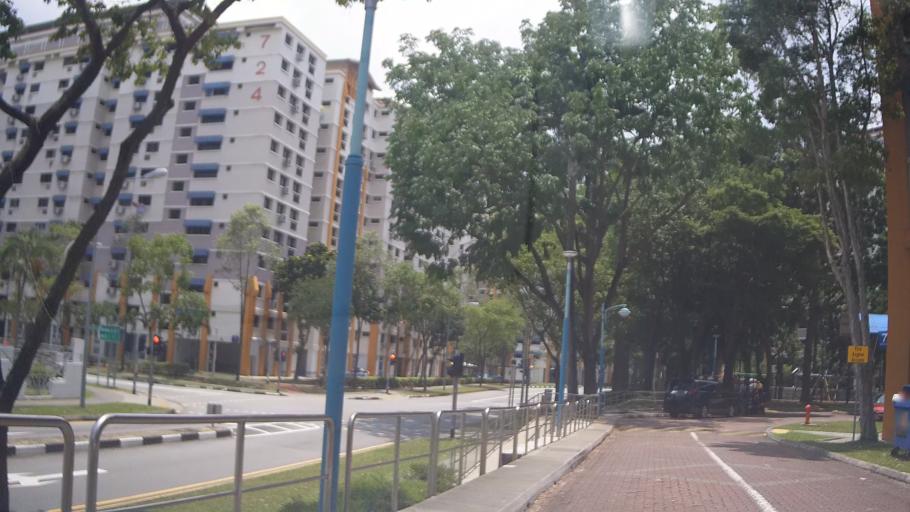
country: MY
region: Johor
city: Johor Bahru
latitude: 1.4444
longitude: 103.7979
